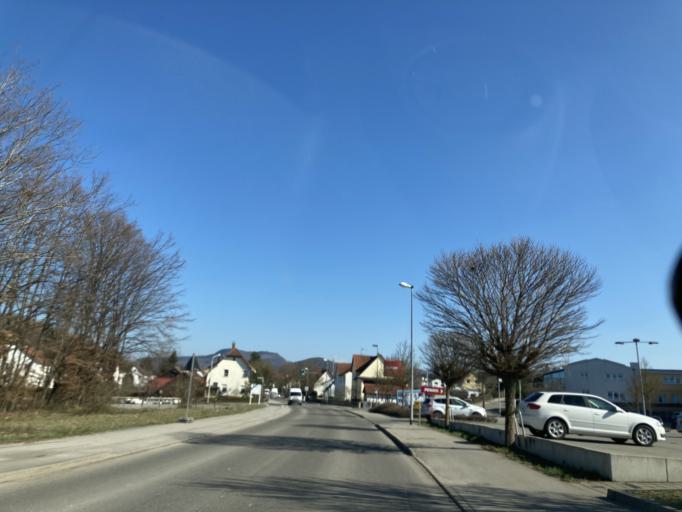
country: DE
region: Baden-Wuerttemberg
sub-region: Tuebingen Region
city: Bodelshausen
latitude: 48.3867
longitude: 8.9805
